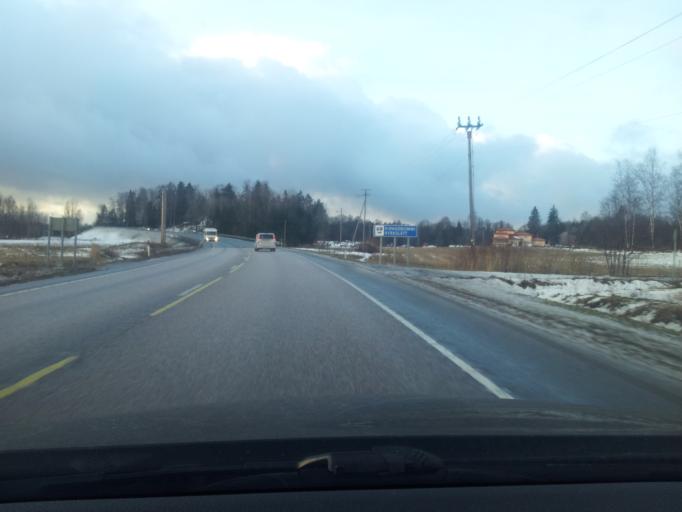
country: FI
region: Uusimaa
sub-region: Helsinki
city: Espoo
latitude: 60.1820
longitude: 24.5604
